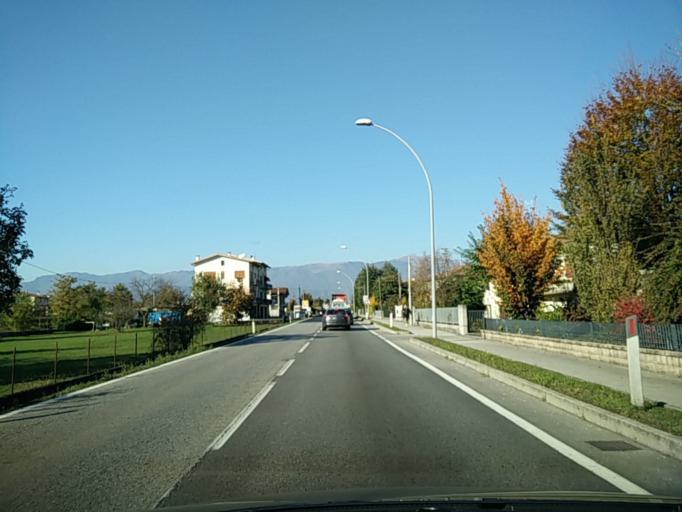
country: IT
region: Veneto
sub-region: Provincia di Treviso
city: San Martino
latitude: 45.9095
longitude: 12.3255
